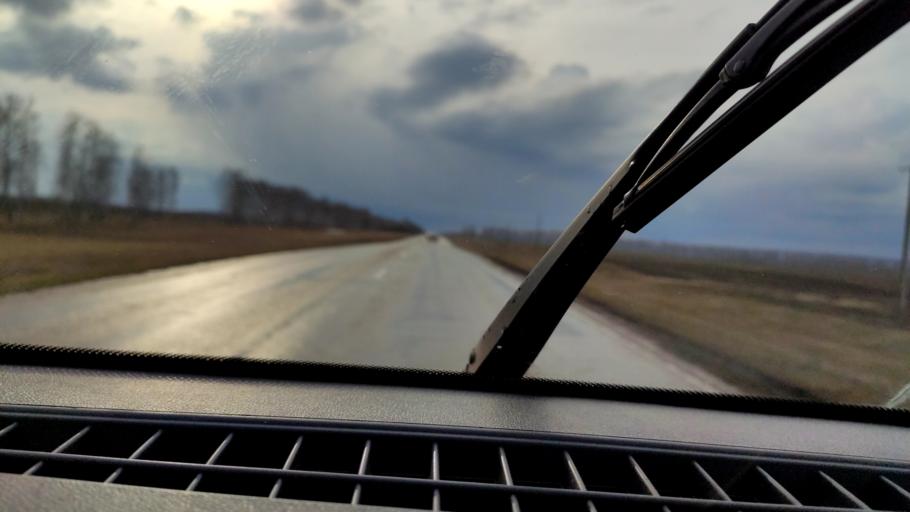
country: RU
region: Bashkortostan
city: Alekseyevka
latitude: 55.1051
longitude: 55.0127
